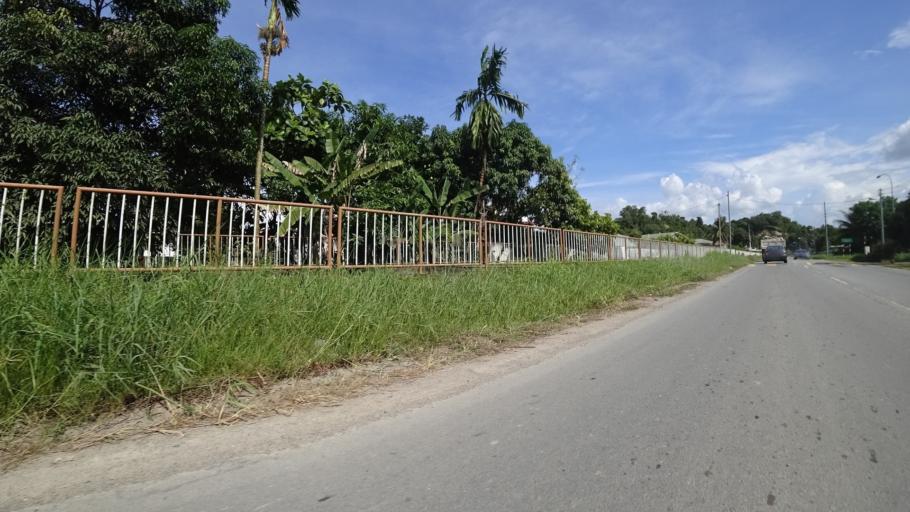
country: BN
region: Brunei and Muara
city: Bandar Seri Begawan
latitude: 4.8830
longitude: 114.8563
